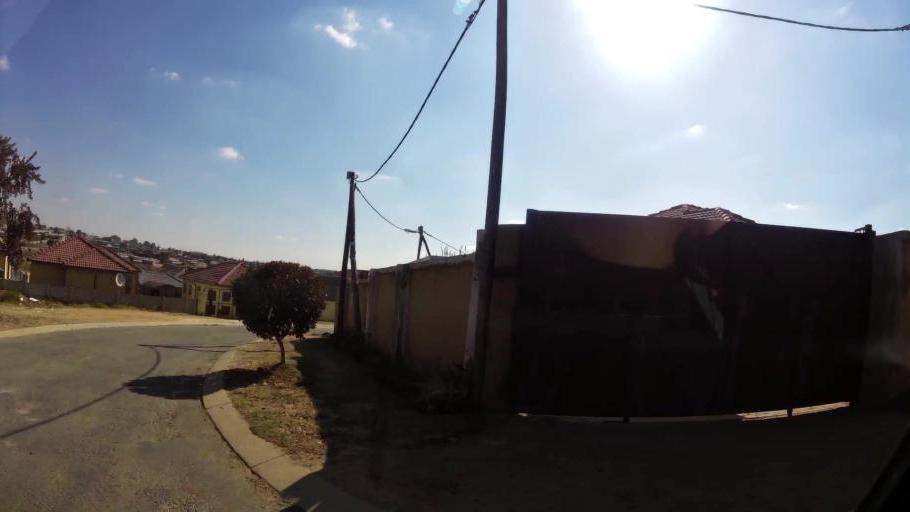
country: ZA
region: Gauteng
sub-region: West Rand District Municipality
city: Muldersdriseloop
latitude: -26.0256
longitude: 27.9340
